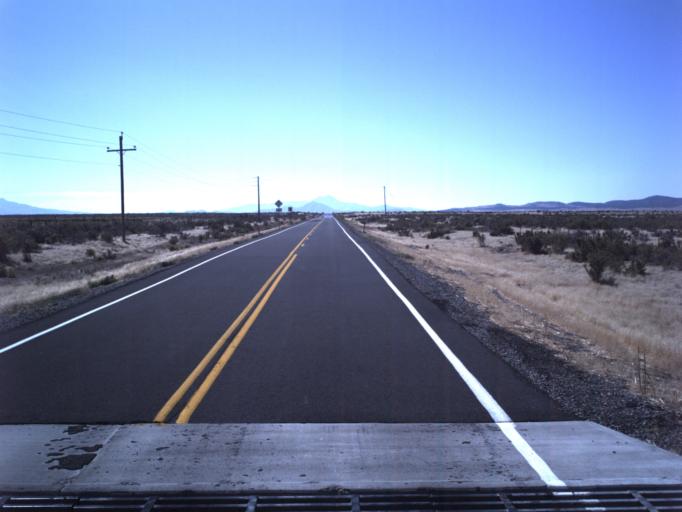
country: US
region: Utah
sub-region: Tooele County
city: Grantsville
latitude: 40.3465
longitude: -112.7452
